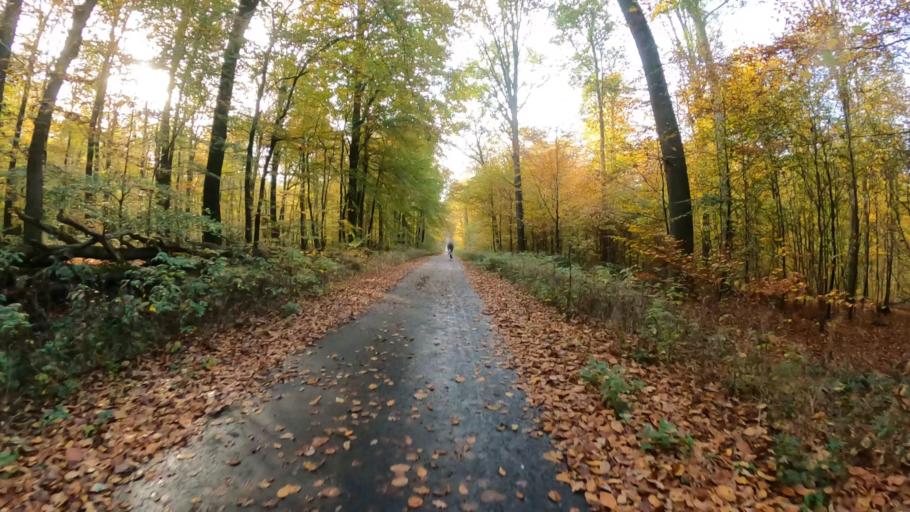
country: DE
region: Lower Saxony
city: Buchholz in der Nordheide
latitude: 53.4012
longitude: 9.8442
